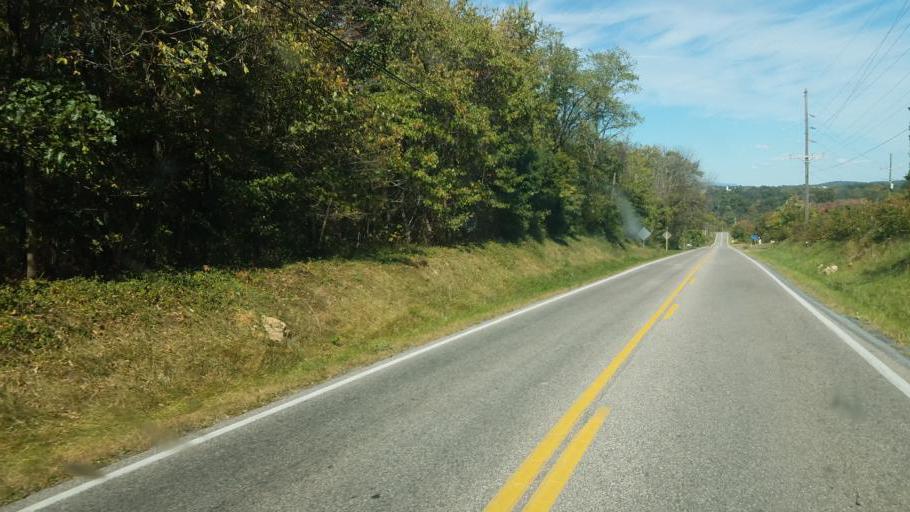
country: US
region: Virginia
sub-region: Page County
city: Shenandoah
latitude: 38.5693
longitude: -78.5976
